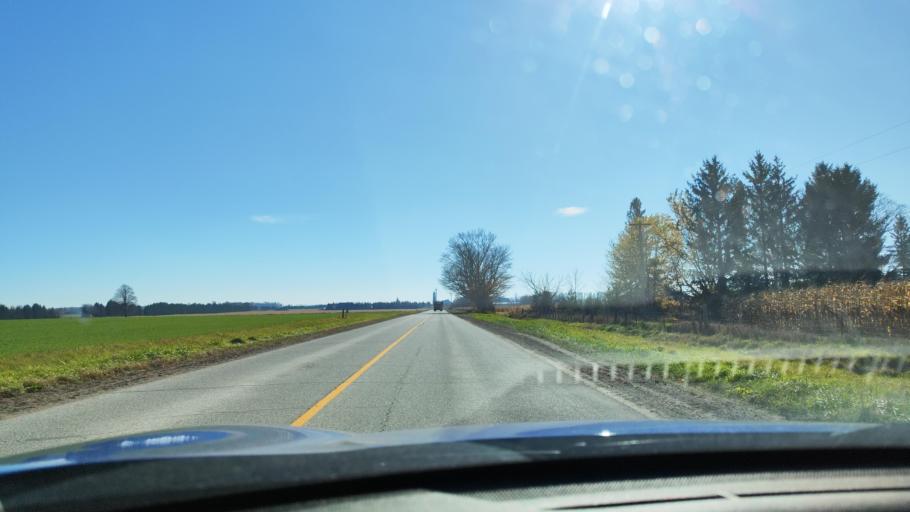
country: CA
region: Ontario
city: Wasaga Beach
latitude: 44.4514
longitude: -80.0012
